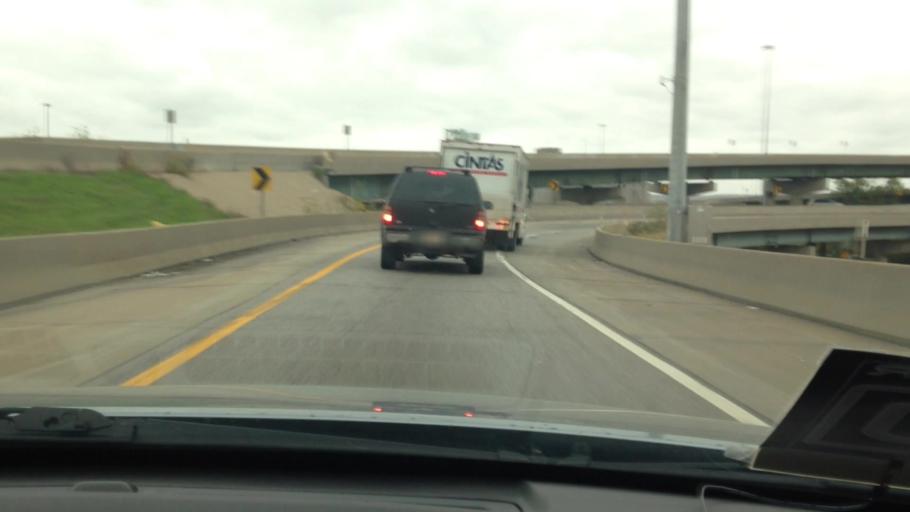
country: US
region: Kansas
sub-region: Wyandotte County
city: Kansas City
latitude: 39.1130
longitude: -94.6178
